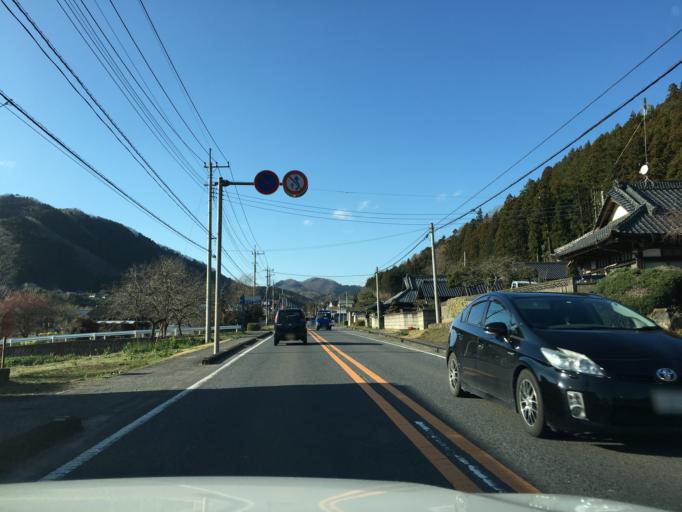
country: JP
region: Ibaraki
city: Omiya
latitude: 36.6590
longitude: 140.3923
